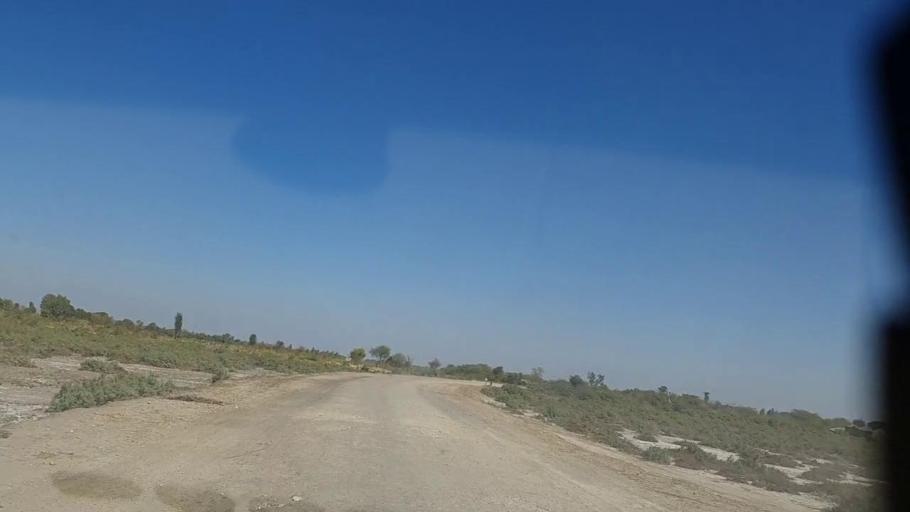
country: PK
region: Sindh
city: Mirwah Gorchani
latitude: 25.2725
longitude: 69.0632
